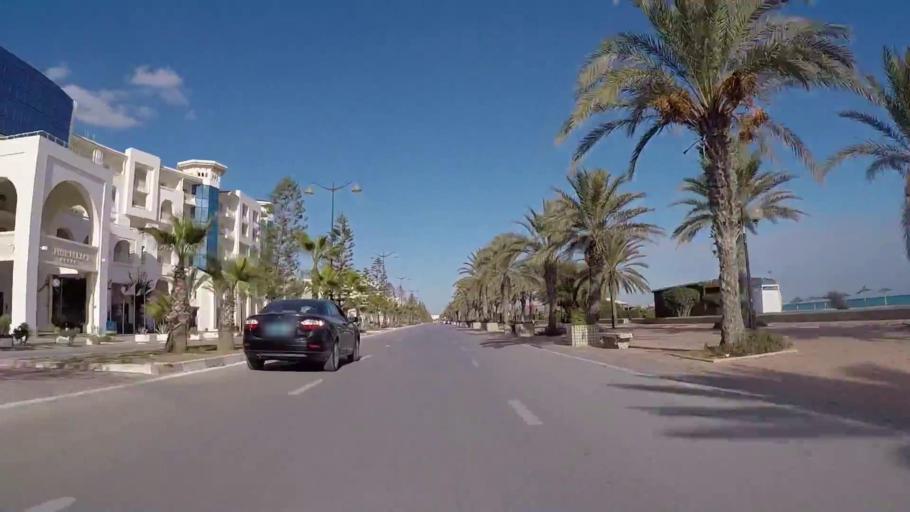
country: TN
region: Nabul
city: Al Hammamat
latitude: 36.3646
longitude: 10.5368
